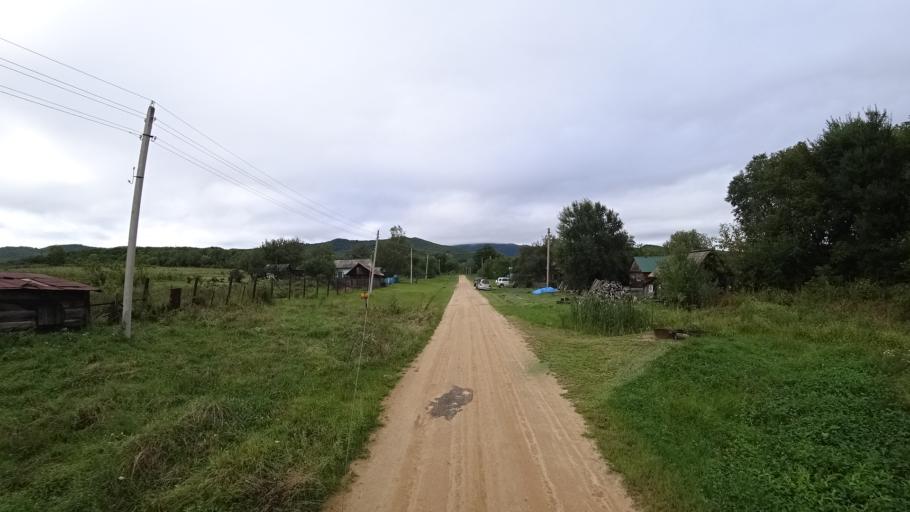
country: RU
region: Primorskiy
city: Rettikhovka
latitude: 44.1389
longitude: 132.6373
